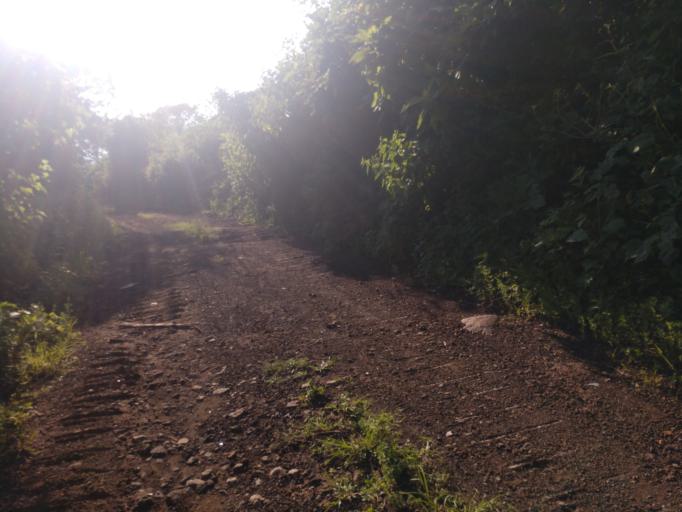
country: MX
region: Nayarit
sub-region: Tepic
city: La Corregidora
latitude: 21.4558
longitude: -104.7831
